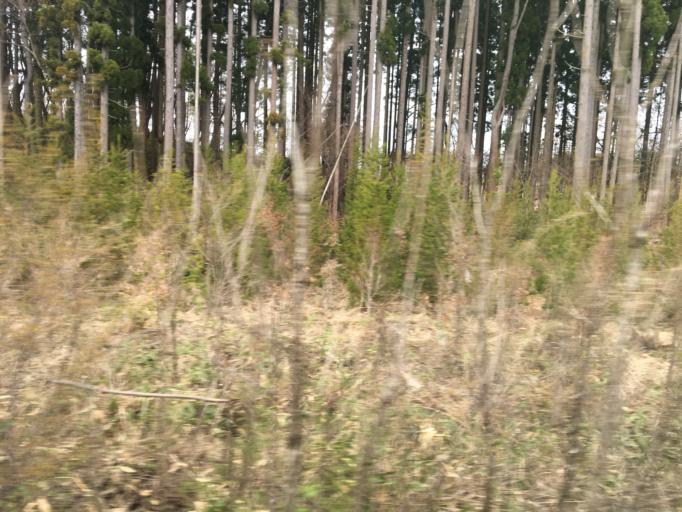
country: JP
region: Aomori
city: Shimokizukuri
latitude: 40.7833
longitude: 140.2828
